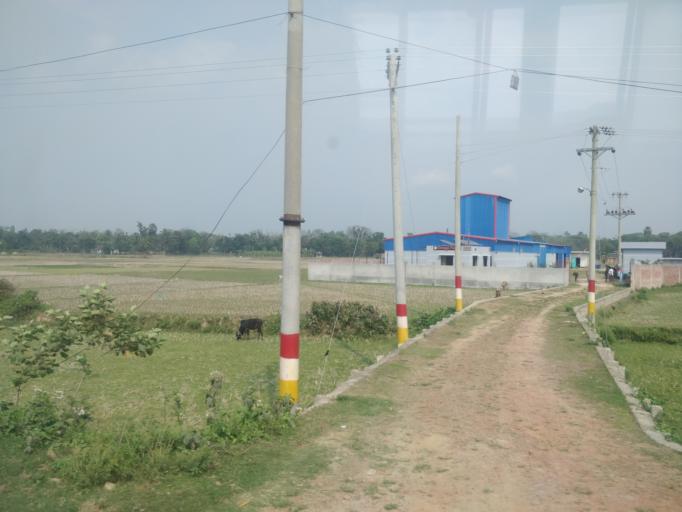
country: BD
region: Sylhet
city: Habiganj
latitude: 24.3180
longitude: 91.4357
